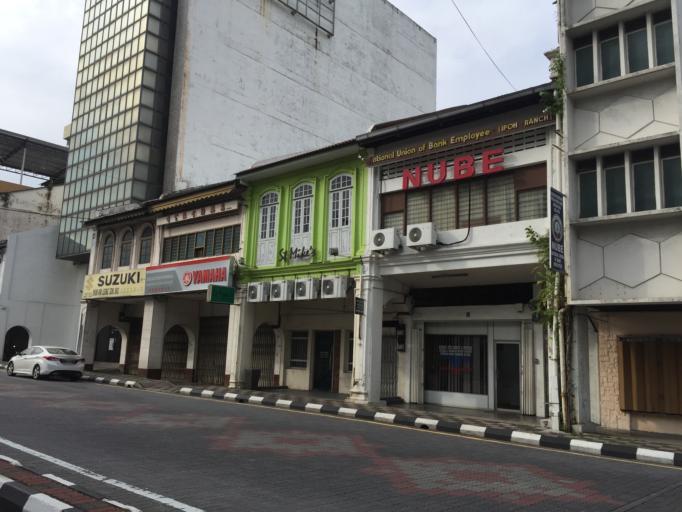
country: MY
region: Perak
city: Ipoh
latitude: 4.5985
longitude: 101.0779
